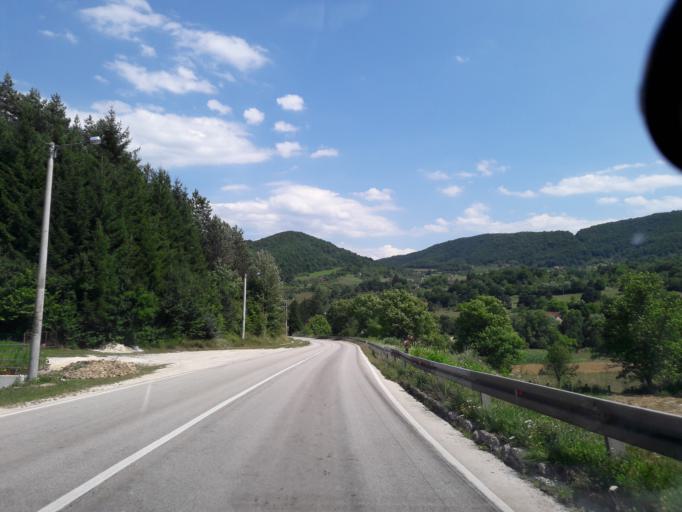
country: BA
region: Republika Srpska
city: Mrkonjic Grad
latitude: 44.4213
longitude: 17.1107
